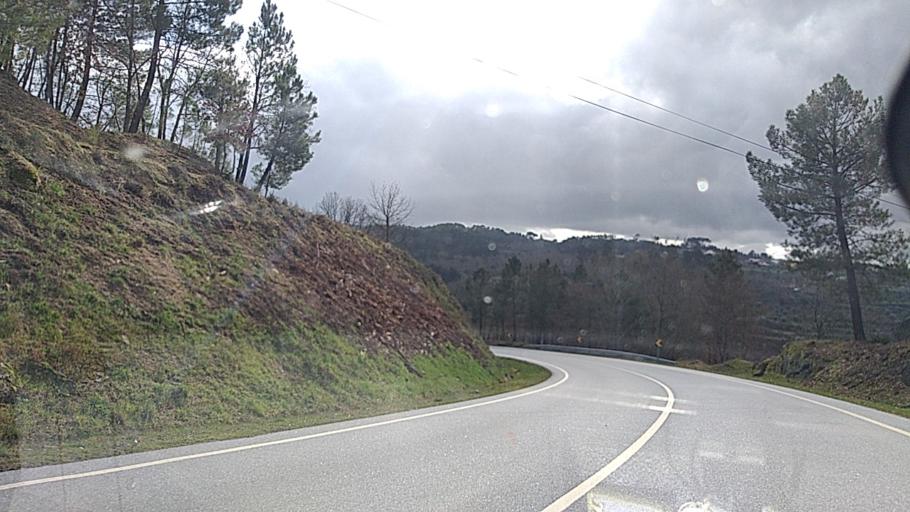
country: PT
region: Viseu
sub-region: Mangualde
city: Mangualde
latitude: 40.6485
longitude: -7.7335
